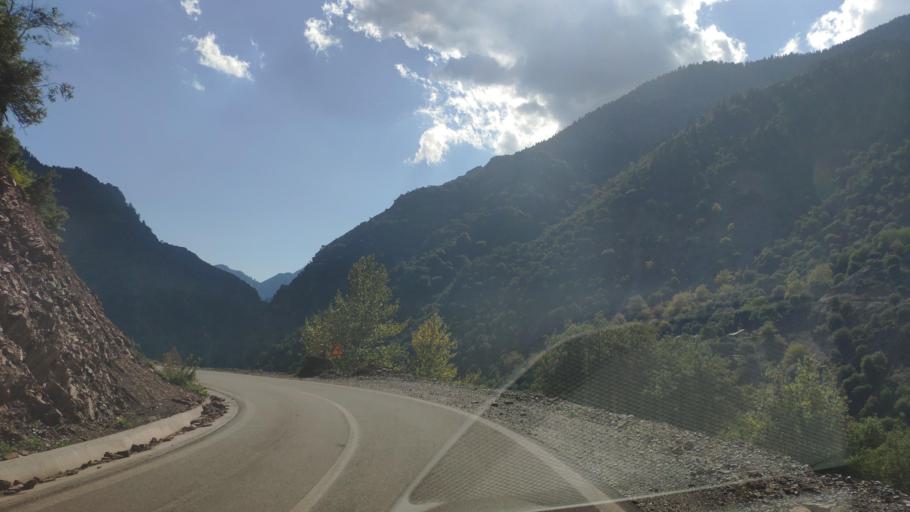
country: GR
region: Central Greece
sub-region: Nomos Evrytanias
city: Kerasochori
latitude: 39.1280
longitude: 21.6267
